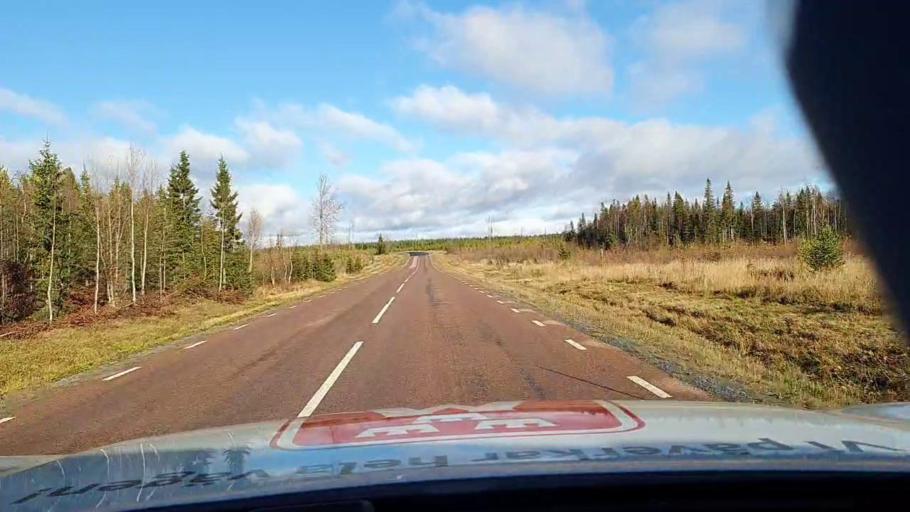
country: SE
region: Jaemtland
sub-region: Krokoms Kommun
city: Valla
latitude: 63.1683
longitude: 13.9977
